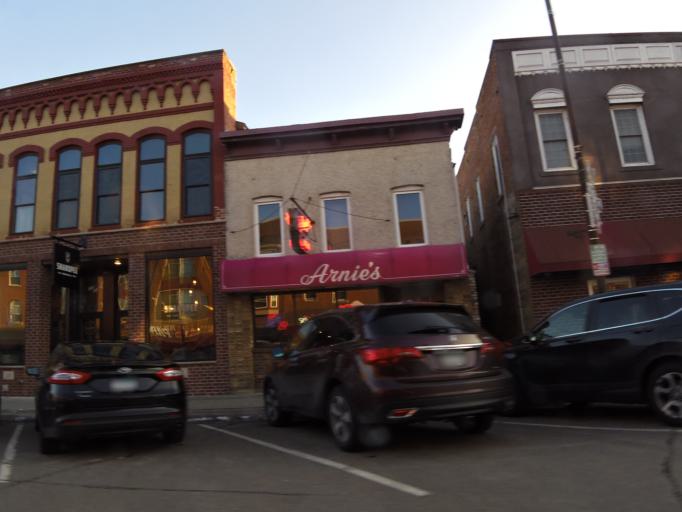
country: US
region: Minnesota
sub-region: Scott County
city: Shakopee
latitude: 44.7987
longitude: -93.5259
